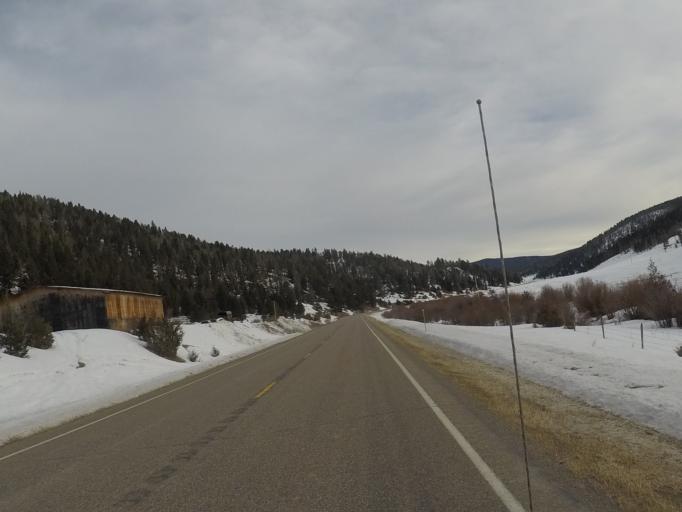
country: US
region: Montana
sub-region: Meagher County
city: White Sulphur Springs
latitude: 46.6882
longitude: -110.8728
